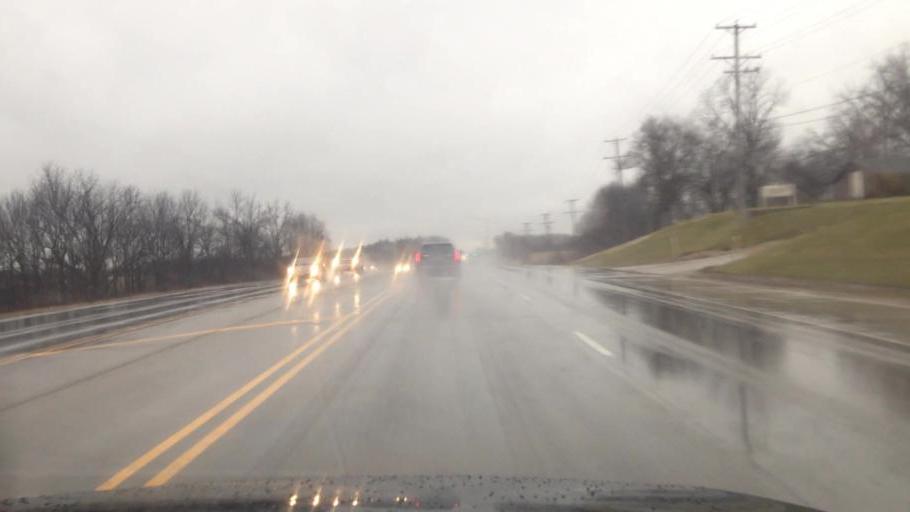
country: US
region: Illinois
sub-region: Kane County
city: Sleepy Hollow
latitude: 42.1119
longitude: -88.3351
